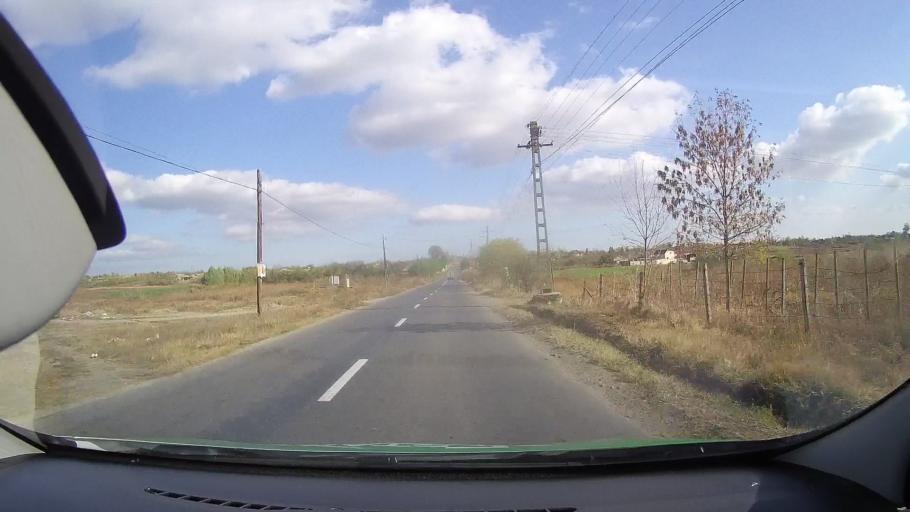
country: RO
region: Constanta
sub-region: Comuna Cogealac
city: Tariverde
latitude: 44.5625
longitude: 28.5947
